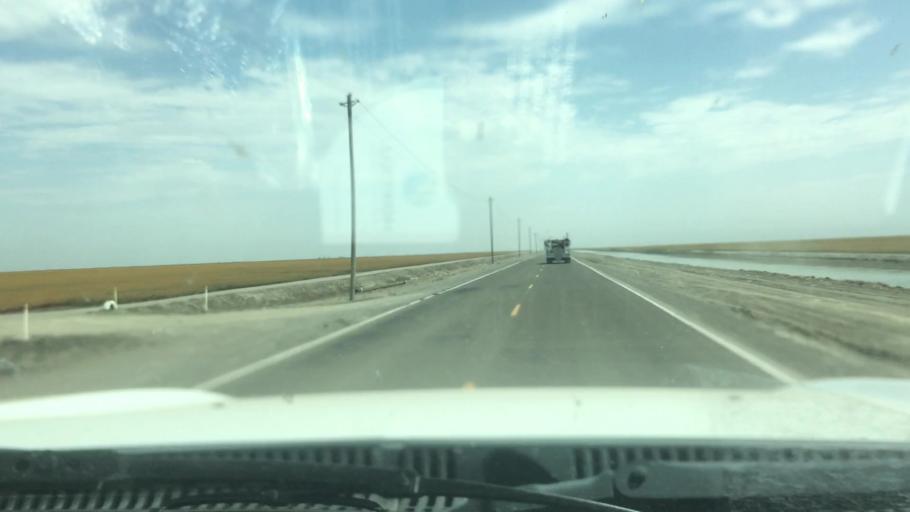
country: US
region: California
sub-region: Tulare County
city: Alpaugh
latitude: 35.9276
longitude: -119.5732
